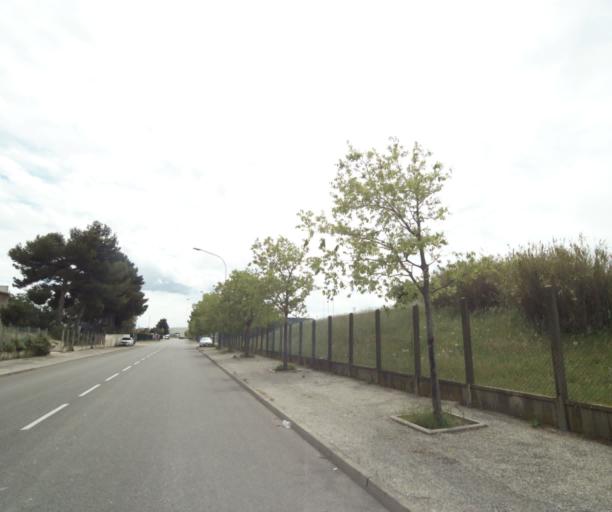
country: FR
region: Provence-Alpes-Cote d'Azur
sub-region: Departement des Bouches-du-Rhone
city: Rognac
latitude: 43.4804
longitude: 5.2350
